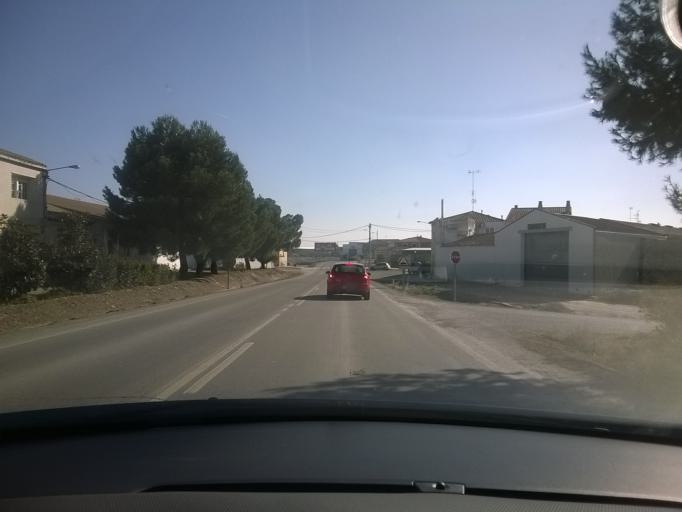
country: ES
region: Aragon
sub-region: Provincia de Zaragoza
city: Bujaraloz
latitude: 41.4985
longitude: -0.1566
